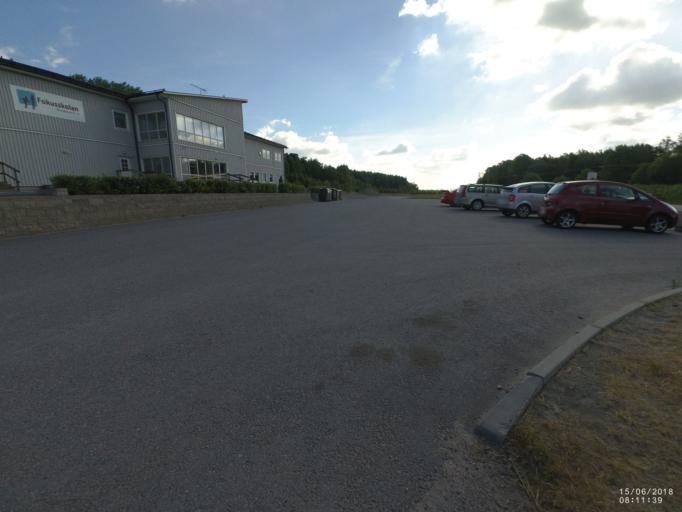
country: SE
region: Soedermanland
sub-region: Nykopings Kommun
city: Nykoping
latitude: 58.7610
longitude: 17.0385
